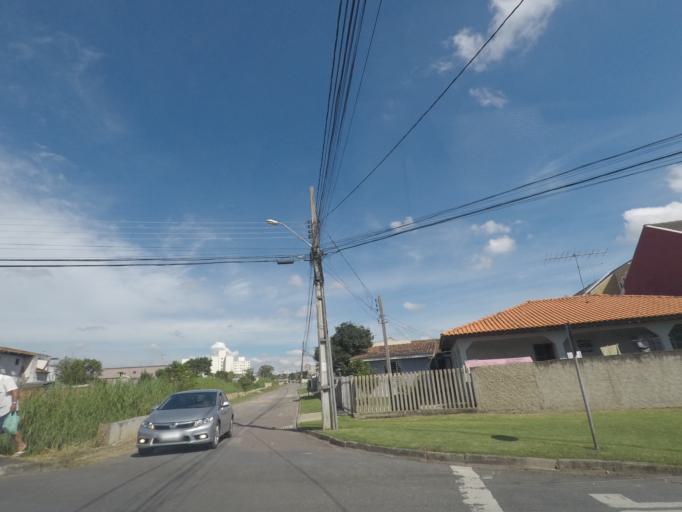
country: BR
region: Parana
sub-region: Curitiba
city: Curitiba
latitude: -25.4774
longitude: -49.2697
